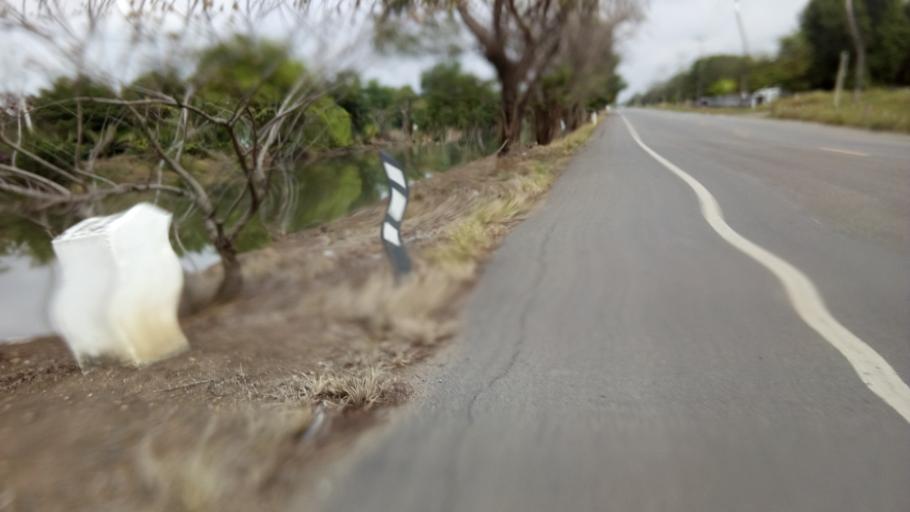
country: TH
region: Pathum Thani
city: Nong Suea
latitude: 14.1702
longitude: 100.8236
